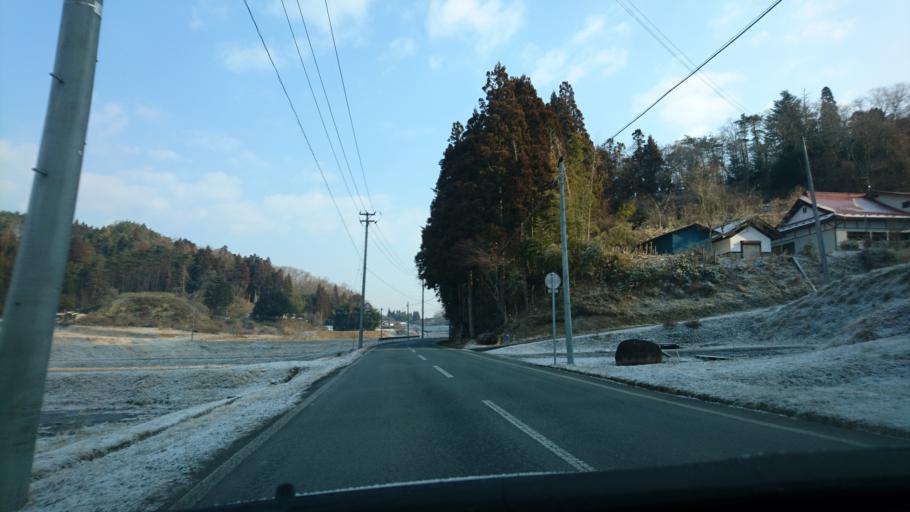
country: JP
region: Iwate
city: Ichinoseki
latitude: 38.9153
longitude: 141.3812
